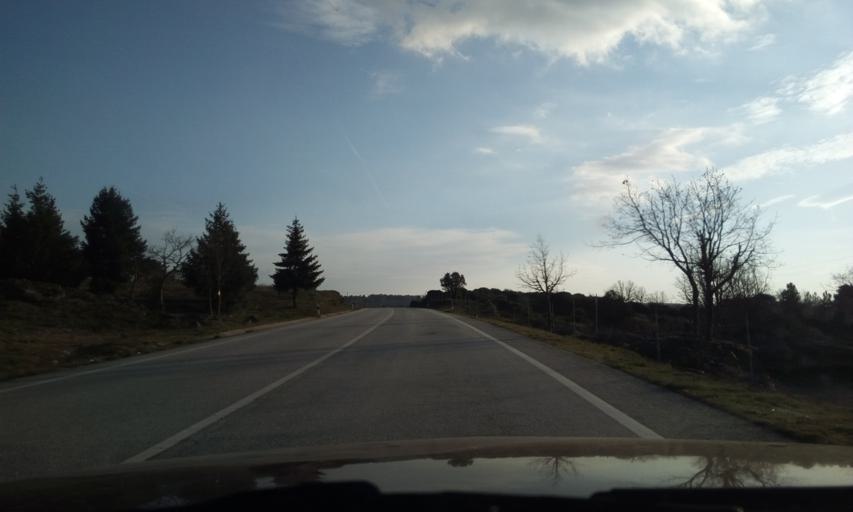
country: ES
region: Castille and Leon
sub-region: Provincia de Salamanca
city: Fuentes de Onoro
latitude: 40.6158
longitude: -6.9814
